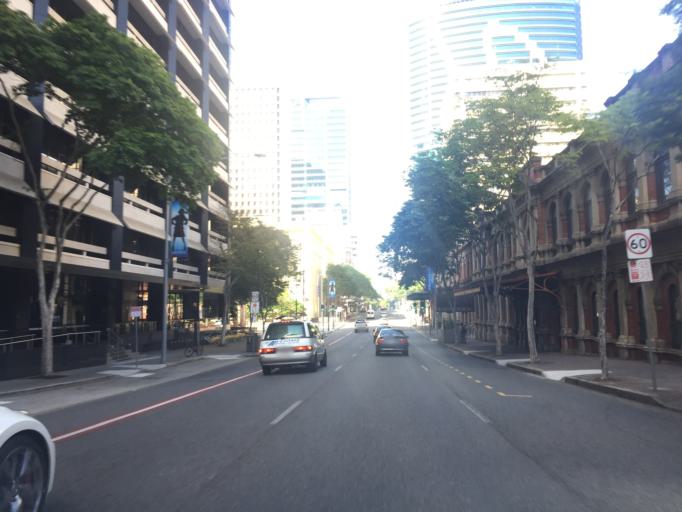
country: AU
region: Queensland
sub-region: Brisbane
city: Brisbane
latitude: -27.4656
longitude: 153.0270
